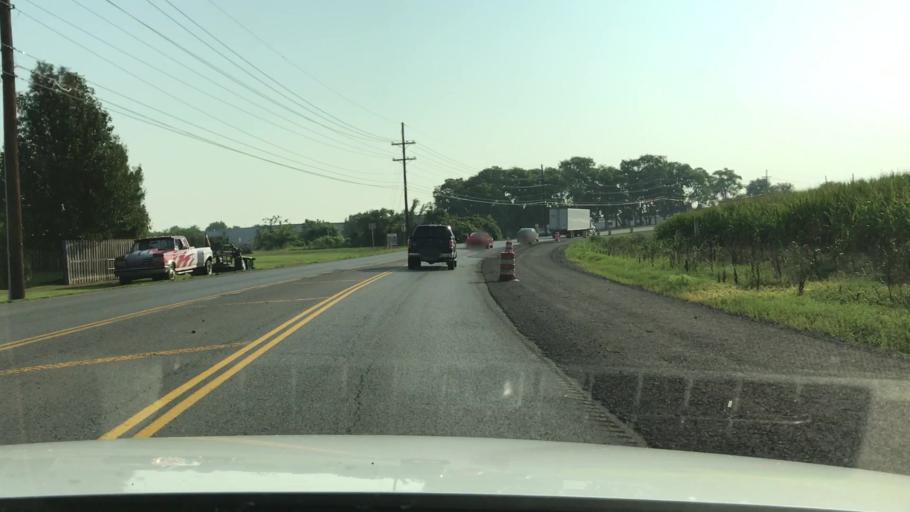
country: US
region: Tennessee
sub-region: Sumner County
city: Gallatin
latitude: 36.3749
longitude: -86.4334
